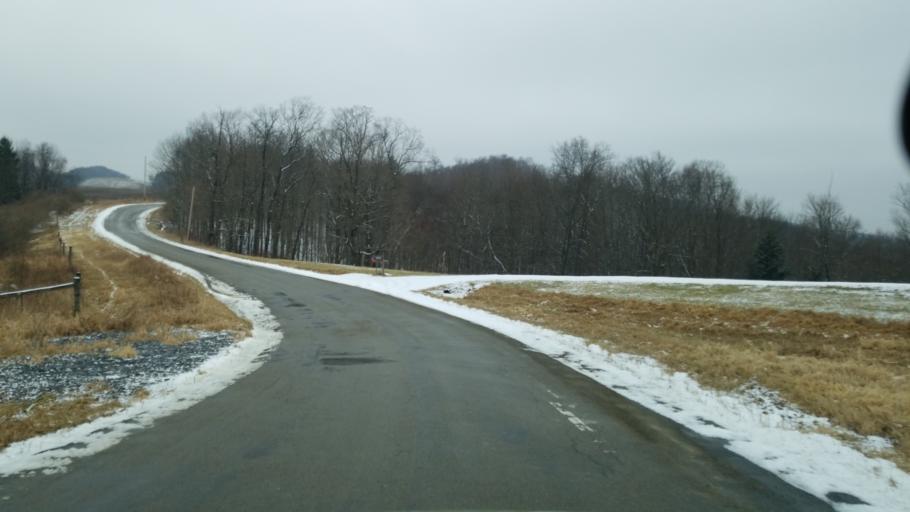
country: US
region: Pennsylvania
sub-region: Jefferson County
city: Sykesville
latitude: 41.0805
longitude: -78.8069
